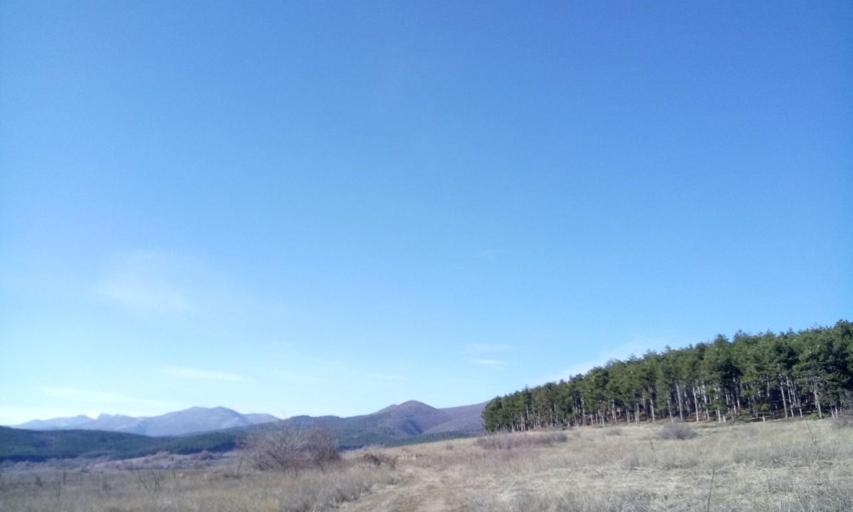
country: BG
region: Plovdiv
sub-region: Obshtina Khisarya
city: Khisarya
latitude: 42.5258
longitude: 24.7131
